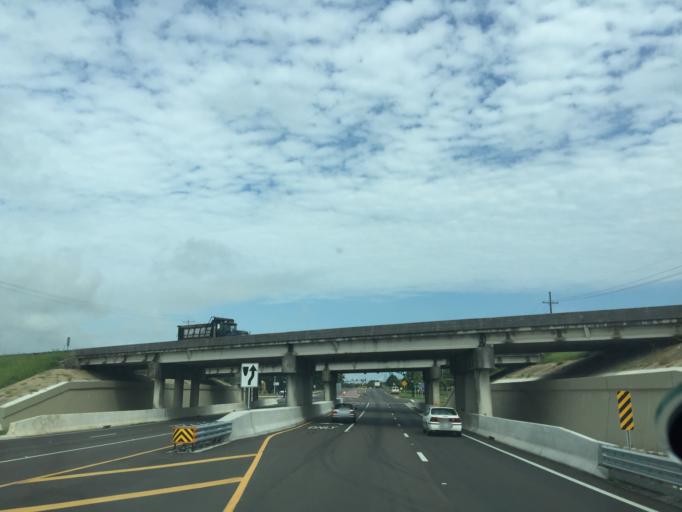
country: US
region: Mississippi
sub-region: Rankin County
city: Brandon
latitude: 32.2785
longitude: -90.0007
